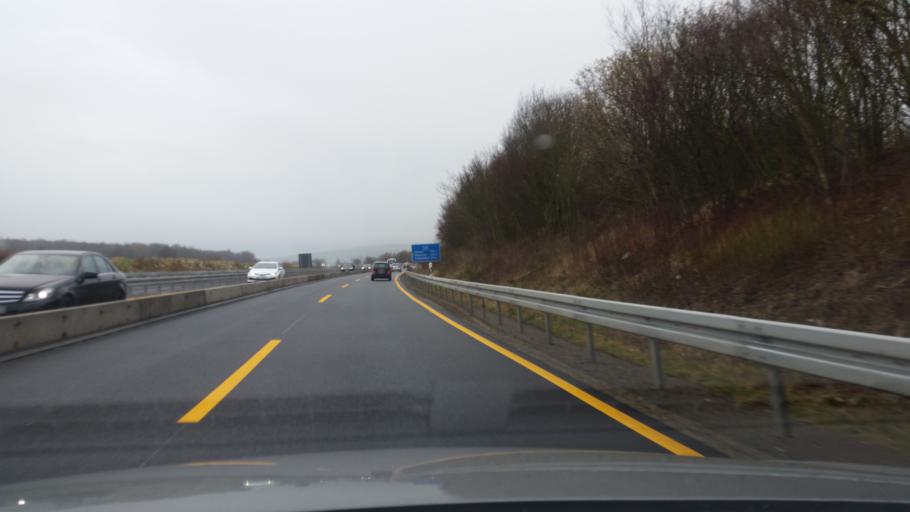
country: DE
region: Lower Saxony
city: Burgdorf
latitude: 52.1200
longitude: 10.2222
